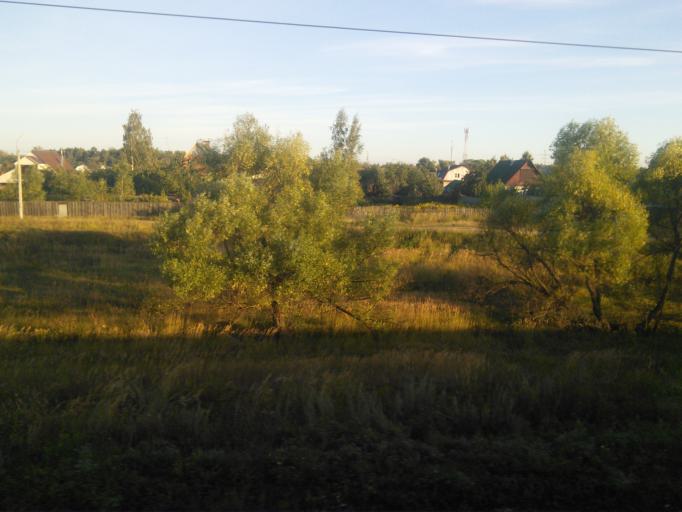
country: RU
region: Moskovskaya
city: Pavlovskiy Posad
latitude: 55.7710
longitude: 38.6373
